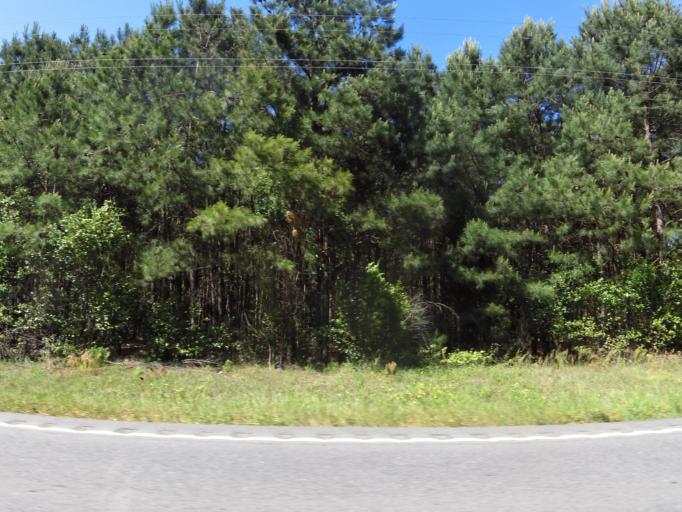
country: US
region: South Carolina
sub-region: Aiken County
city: Aiken
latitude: 33.5196
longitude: -81.6002
